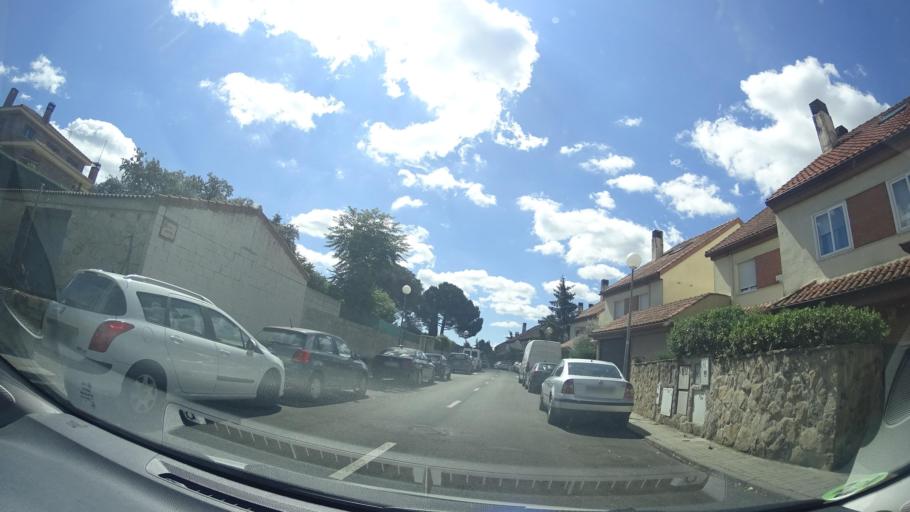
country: ES
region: Madrid
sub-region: Provincia de Madrid
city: Collado-Villalba
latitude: 40.6252
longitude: -3.9989
